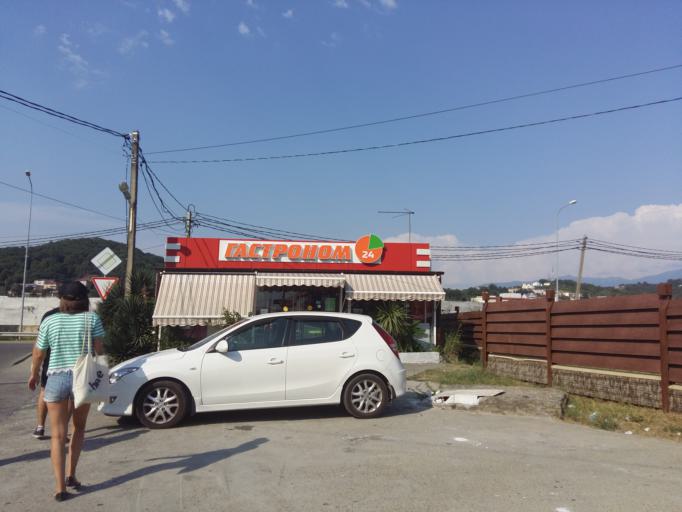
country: RU
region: Krasnodarskiy
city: Adler
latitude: 43.4150
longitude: 39.9565
